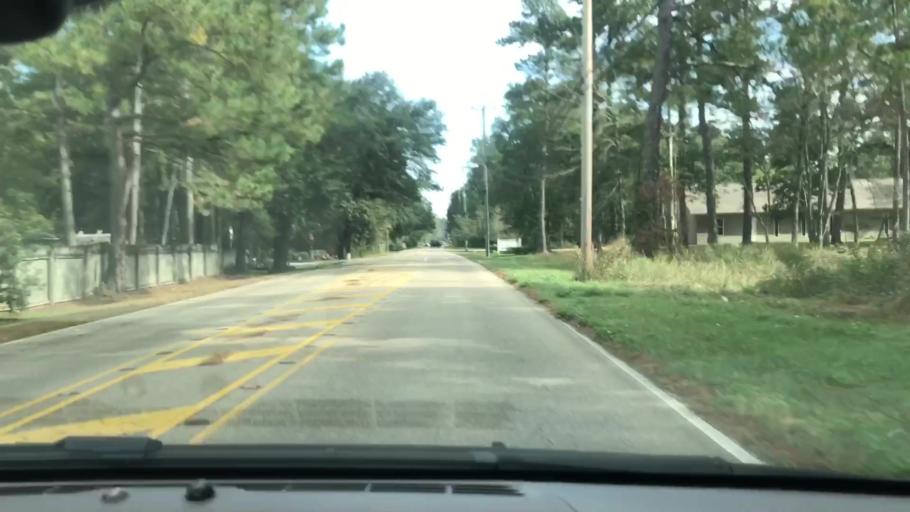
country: US
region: Louisiana
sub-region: Saint Tammany Parish
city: Abita Springs
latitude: 30.4599
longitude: -90.0513
